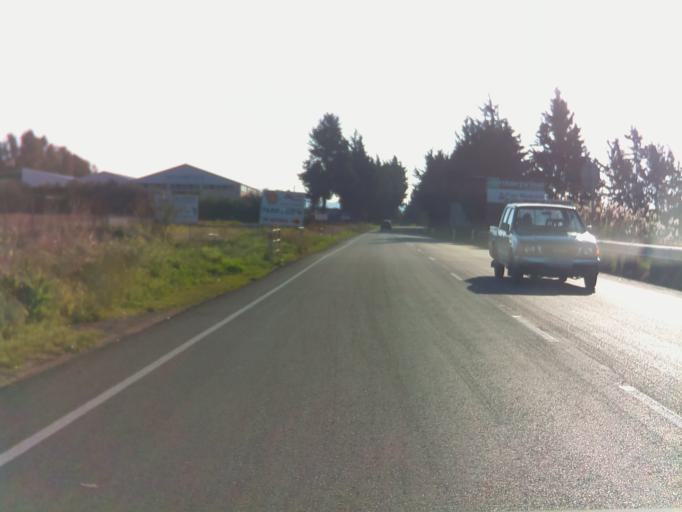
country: CY
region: Pafos
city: Paphos
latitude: 34.7262
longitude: 32.5195
